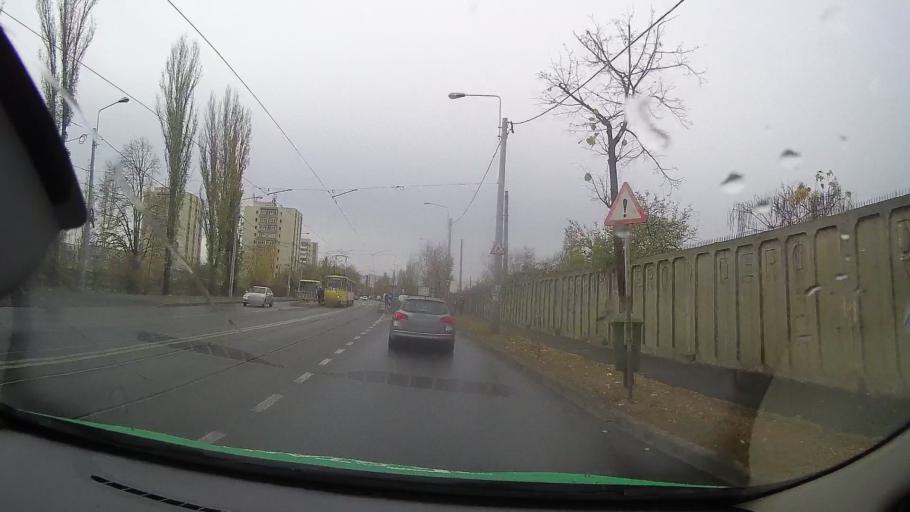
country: RO
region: Prahova
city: Ploiesti
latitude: 44.9496
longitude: 25.9974
